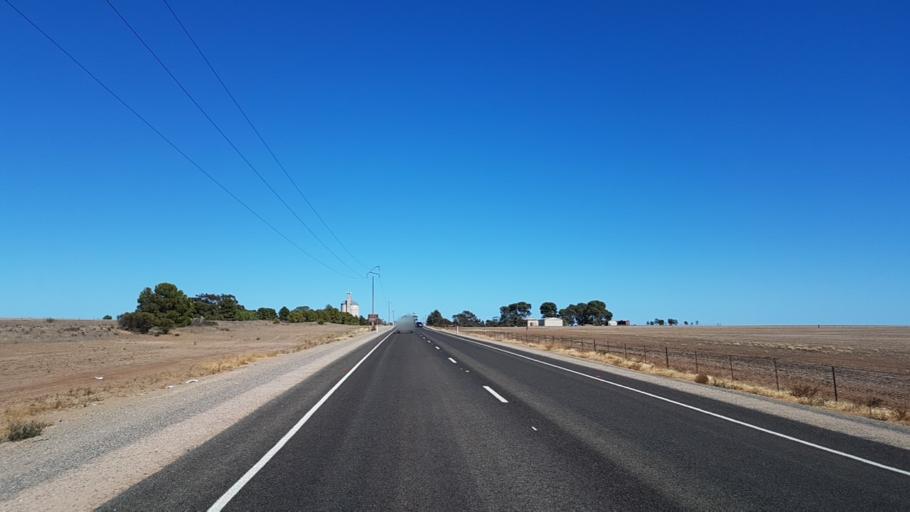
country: AU
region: South Australia
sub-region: Copper Coast
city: Kadina
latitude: -34.0403
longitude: 137.9143
